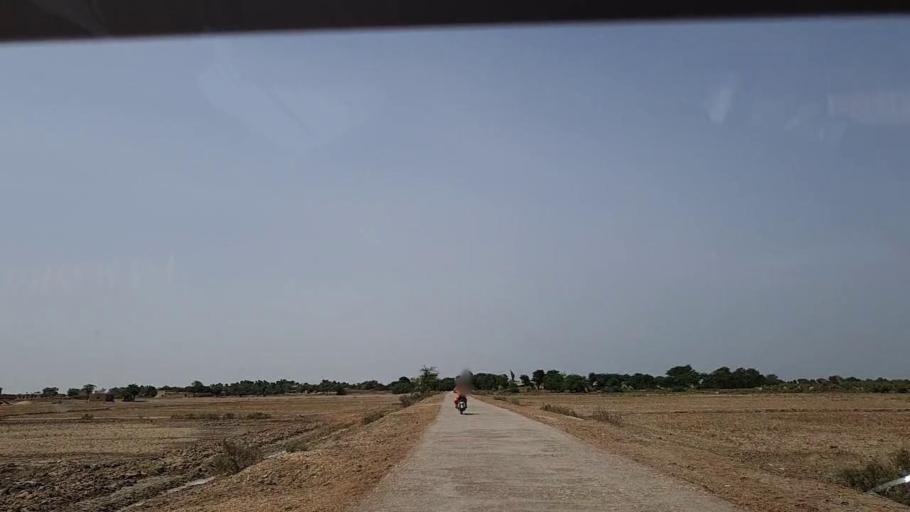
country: PK
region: Sindh
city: Johi
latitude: 26.7787
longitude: 67.6201
